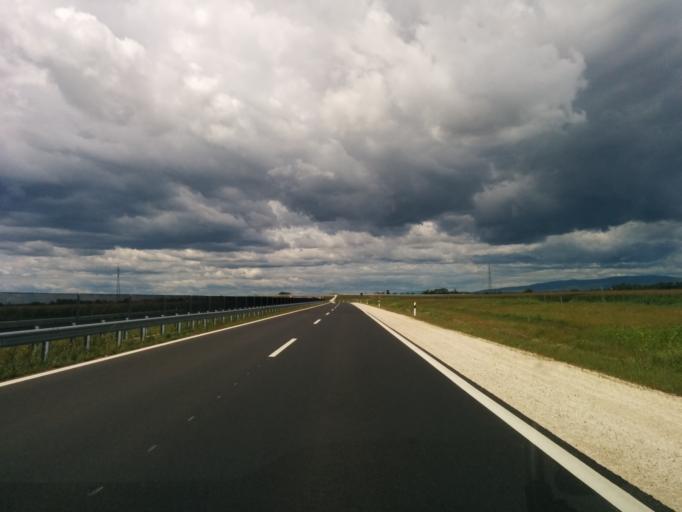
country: HU
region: Vas
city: Vep
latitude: 47.2552
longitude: 16.7054
